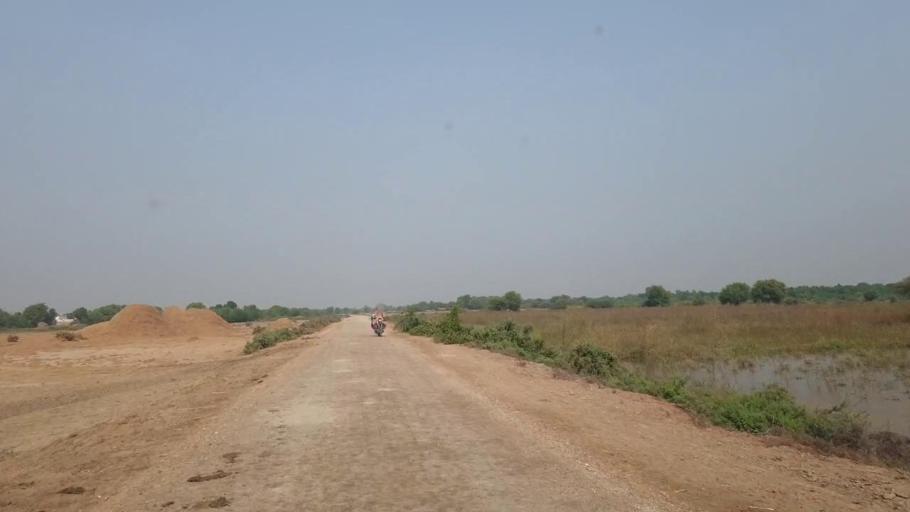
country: PK
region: Sindh
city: Matli
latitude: 25.1582
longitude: 68.7295
